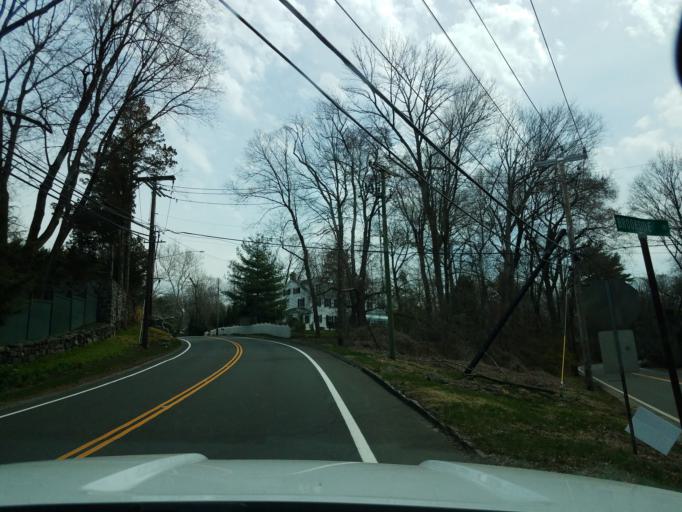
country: US
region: Connecticut
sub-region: Fairfield County
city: Greenwich
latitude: 41.0309
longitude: -73.6384
